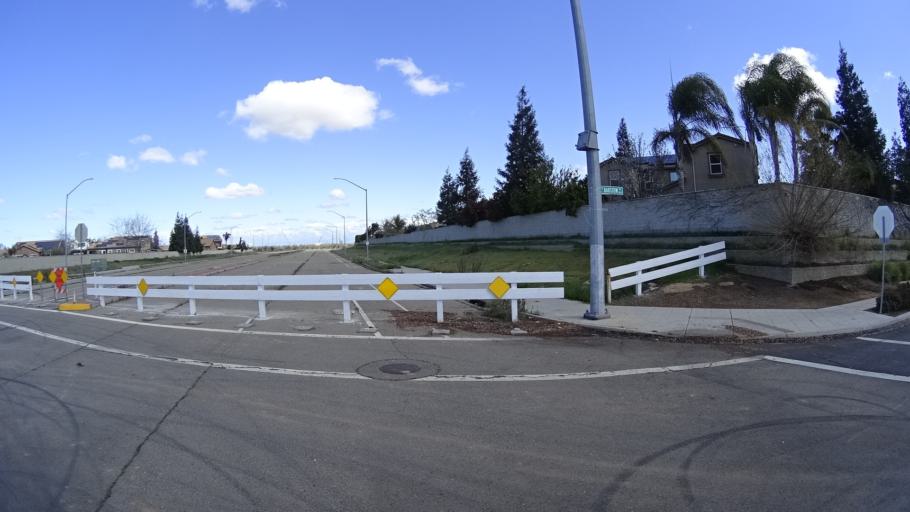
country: US
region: California
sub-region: Fresno County
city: Biola
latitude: 36.8162
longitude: -119.9067
